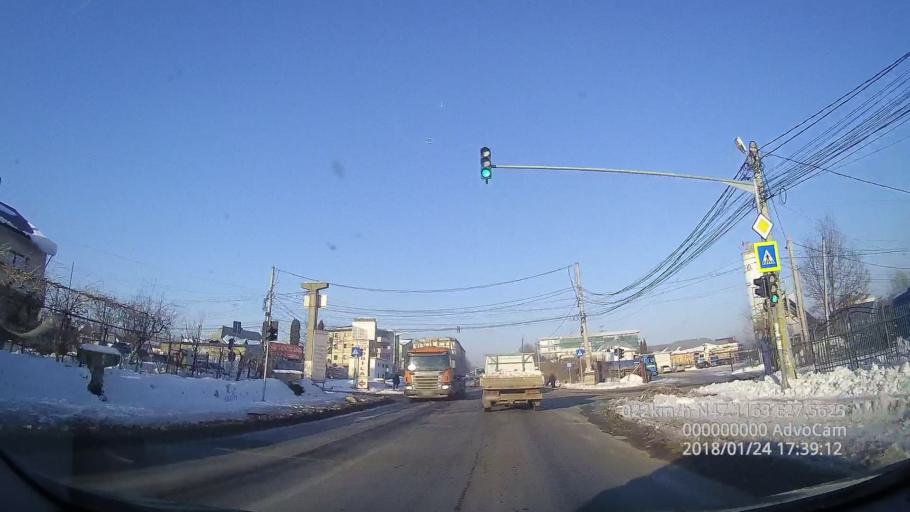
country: RO
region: Iasi
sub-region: Comuna Ciurea
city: Lunca Cetatuii
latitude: 47.1165
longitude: 27.5626
